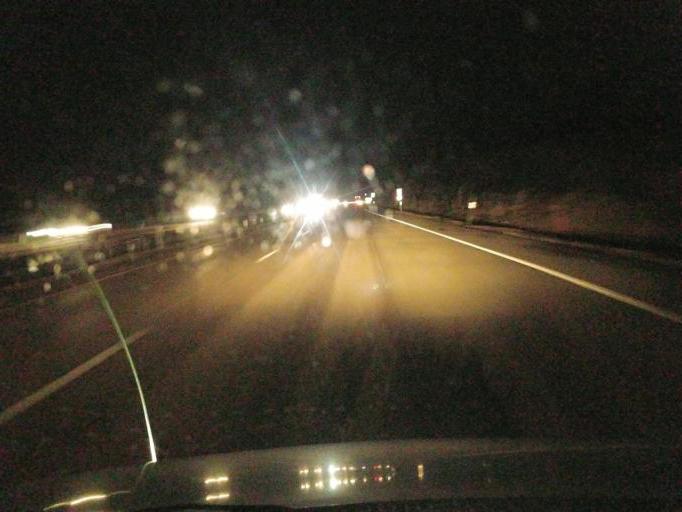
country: US
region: Missouri
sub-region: Franklin County
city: Villa Ridge
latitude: 38.4700
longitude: -90.8529
